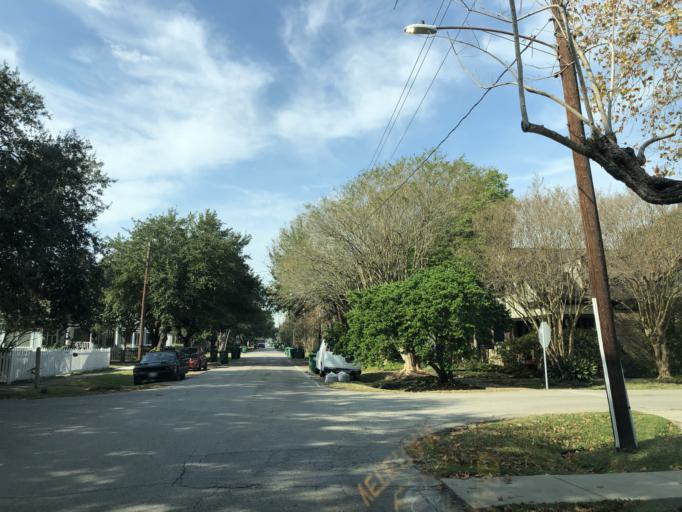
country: US
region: Texas
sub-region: Harris County
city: Houston
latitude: 29.7943
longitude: -95.3999
